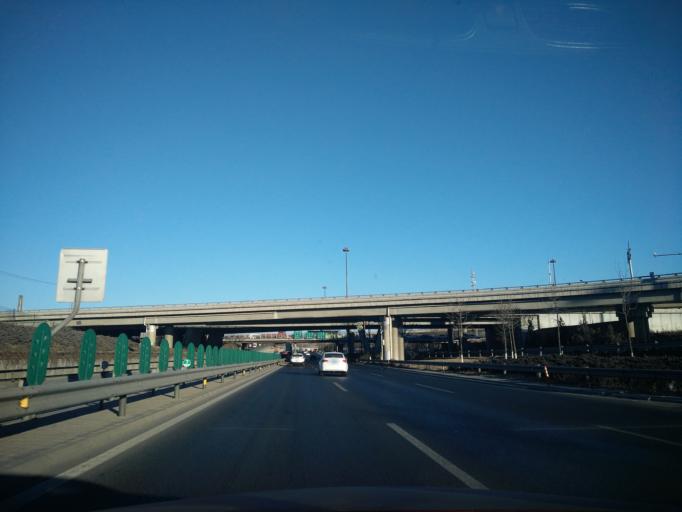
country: CN
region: Beijing
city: Fengtai
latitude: 39.8434
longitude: 116.2198
